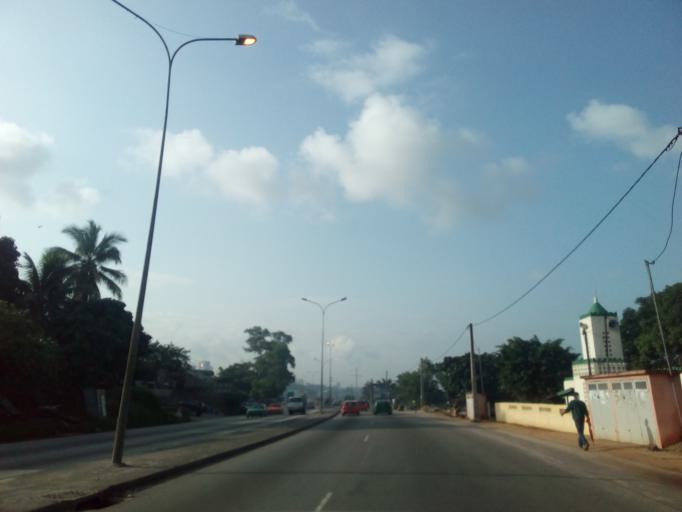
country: CI
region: Lagunes
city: Abidjan
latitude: 5.3459
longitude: -4.0389
